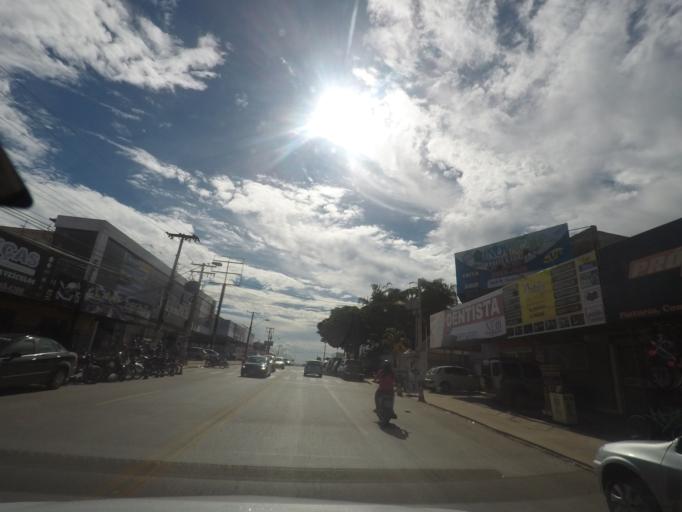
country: BR
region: Goias
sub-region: Aparecida De Goiania
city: Aparecida de Goiania
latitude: -16.8239
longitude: -49.2823
